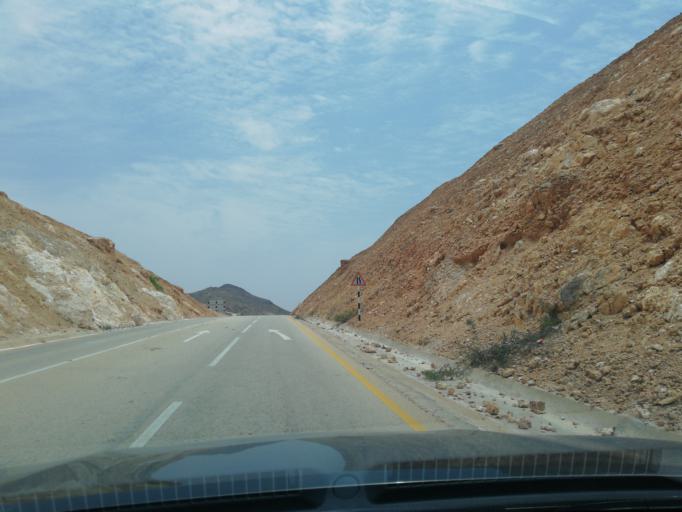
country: OM
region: Zufar
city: Salalah
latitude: 16.8754
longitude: 53.7301
